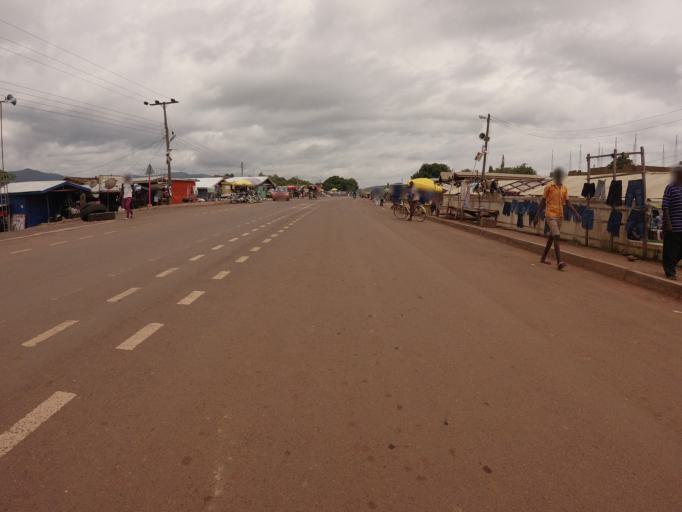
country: TG
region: Centrale
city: Sotouboua
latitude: 8.2615
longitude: 0.5215
